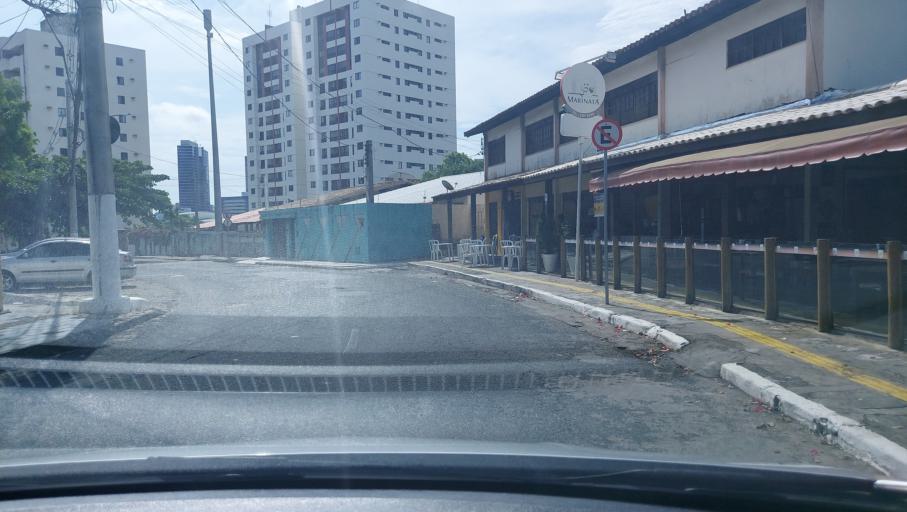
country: BR
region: Bahia
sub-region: Salvador
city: Salvador
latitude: -12.9825
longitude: -38.4474
